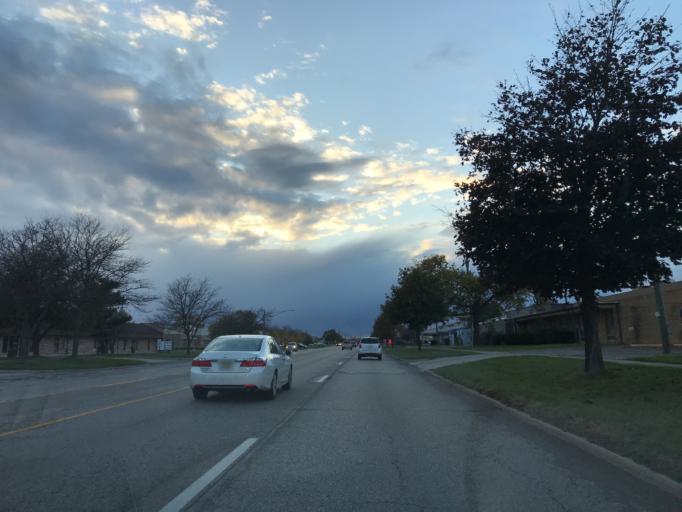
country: US
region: Michigan
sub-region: Oakland County
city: Farmington
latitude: 42.4408
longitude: -83.3707
